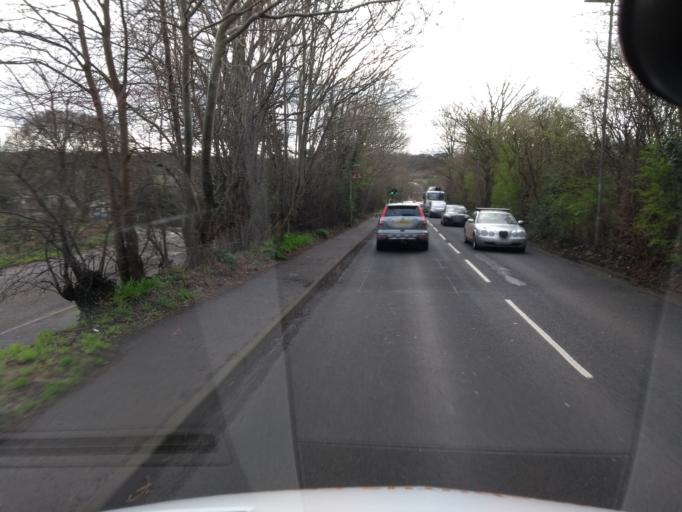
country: GB
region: England
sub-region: Somerset
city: Yeovil
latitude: 50.9445
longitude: -2.6154
